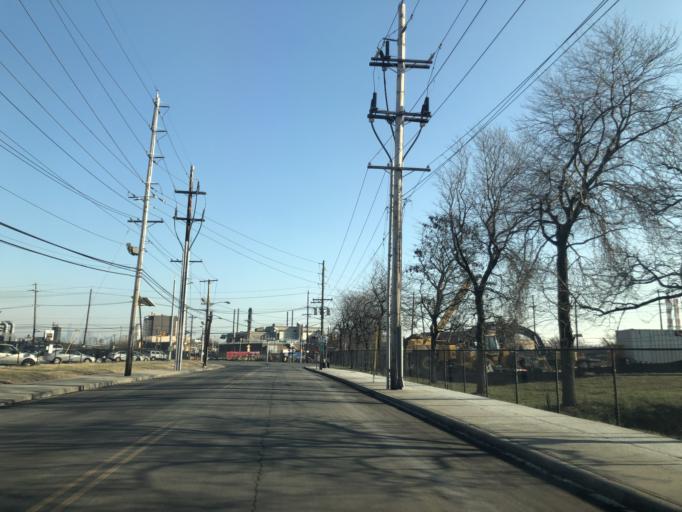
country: US
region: New Jersey
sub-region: Hudson County
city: Harrison
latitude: 40.7136
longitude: -74.1316
